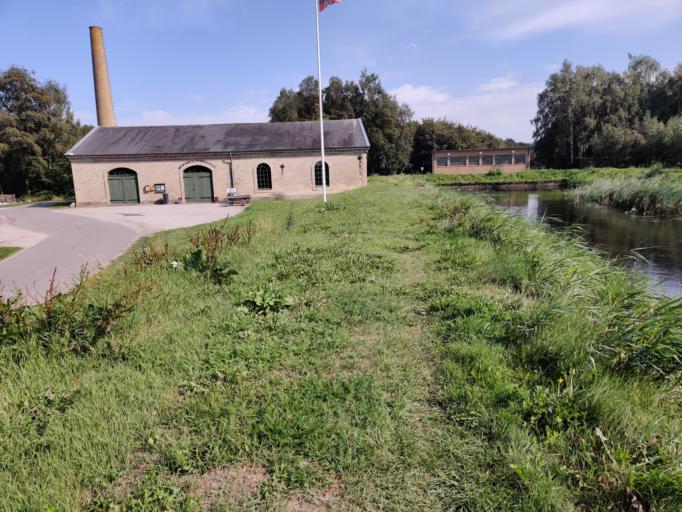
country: DK
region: Zealand
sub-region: Guldborgsund Kommune
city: Nykobing Falster
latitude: 54.6825
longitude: 11.9077
